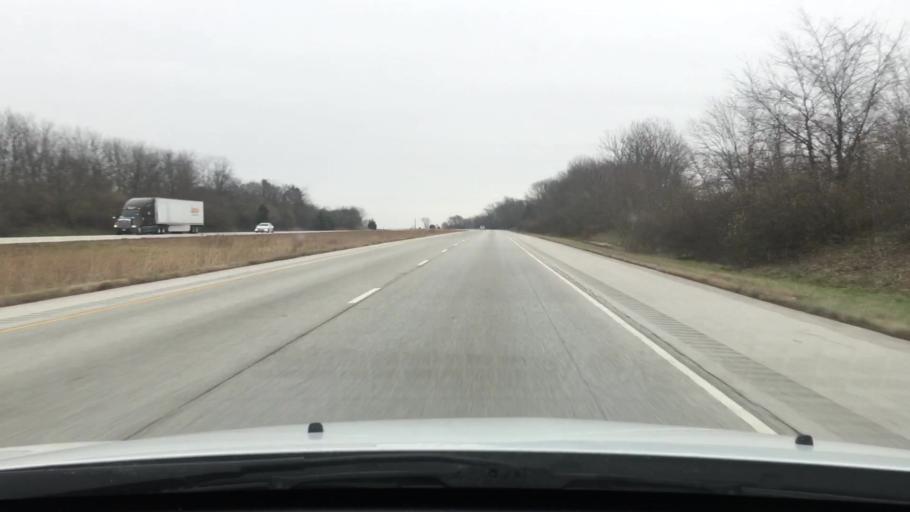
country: US
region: Illinois
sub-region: Scott County
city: Winchester
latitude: 39.6807
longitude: -90.3908
